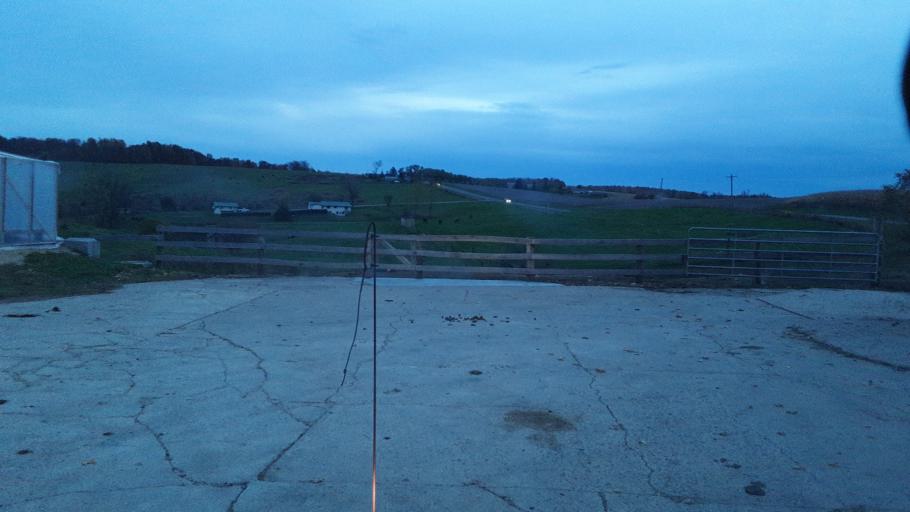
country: US
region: Wisconsin
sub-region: Vernon County
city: Hillsboro
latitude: 43.6593
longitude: -90.4574
